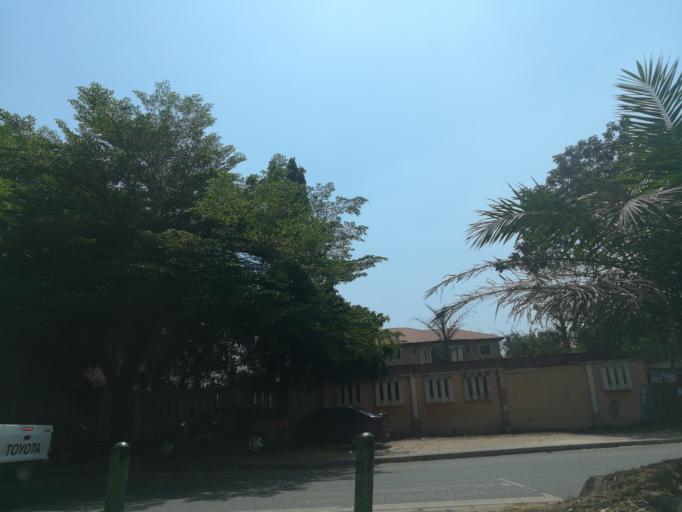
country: NG
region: Abuja Federal Capital Territory
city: Abuja
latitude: 9.0716
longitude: 7.4441
